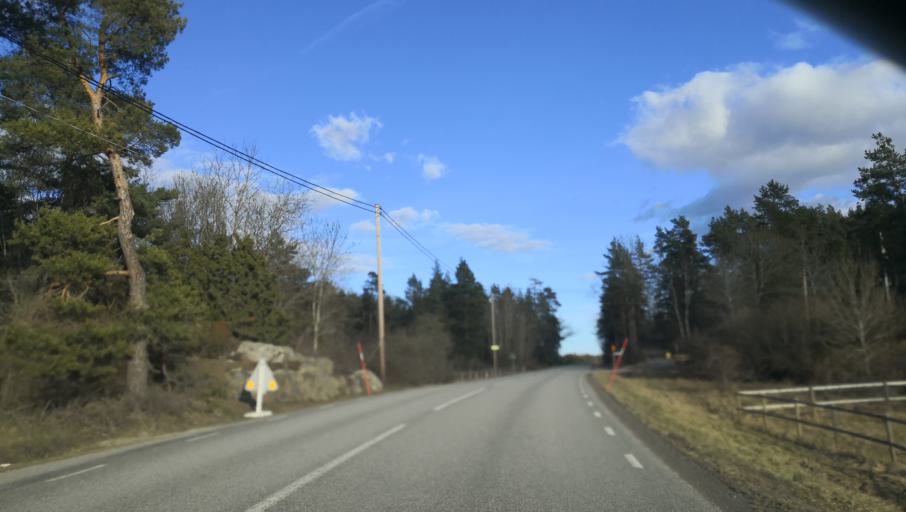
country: SE
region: Stockholm
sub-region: Varmdo Kommun
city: Gustavsberg
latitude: 59.3492
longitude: 18.3699
